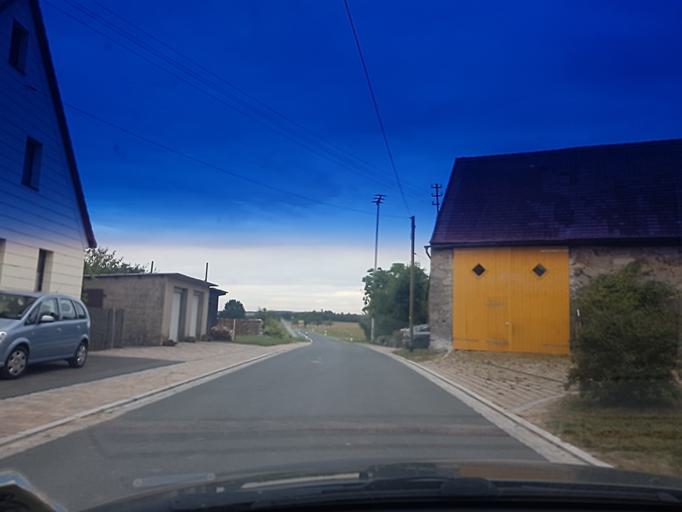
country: DE
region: Bavaria
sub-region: Regierungsbezirk Unterfranken
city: Geiselwind
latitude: 49.7984
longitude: 10.4881
